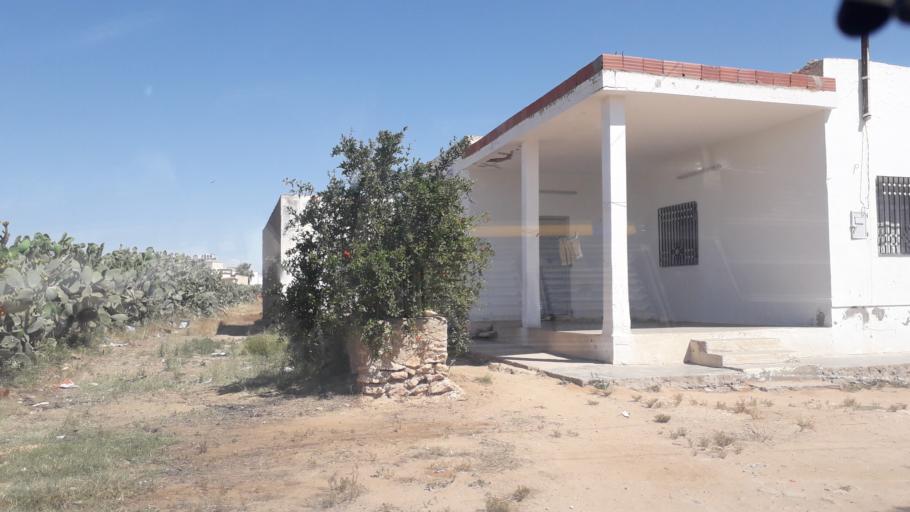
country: TN
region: Safaqis
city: Al Qarmadah
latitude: 34.8298
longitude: 10.7663
